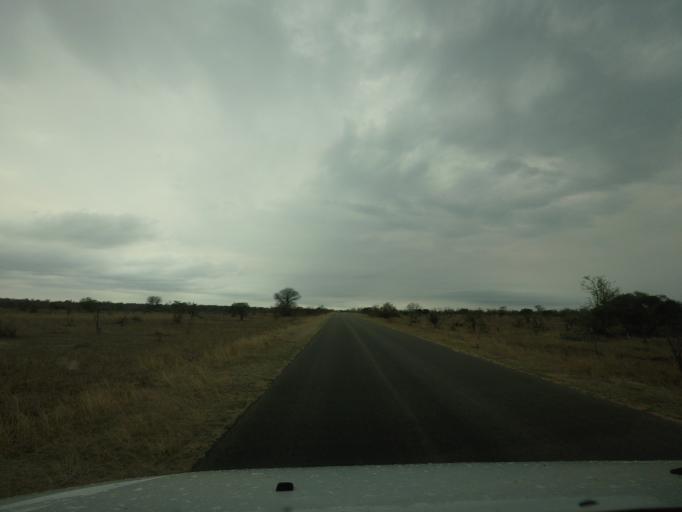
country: ZA
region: Limpopo
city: Thulamahashi
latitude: -24.4686
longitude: 31.4456
